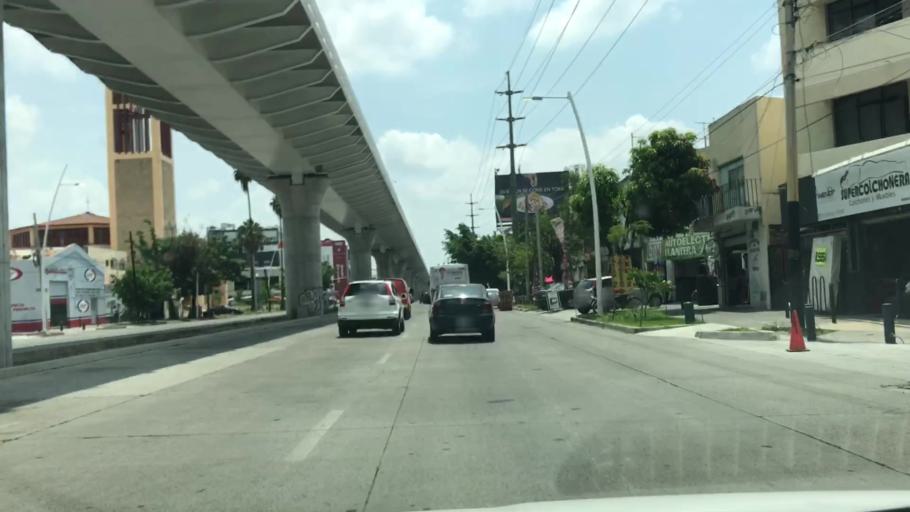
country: MX
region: Jalisco
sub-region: Zapopan
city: Zapopan
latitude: 20.7033
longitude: -103.3613
